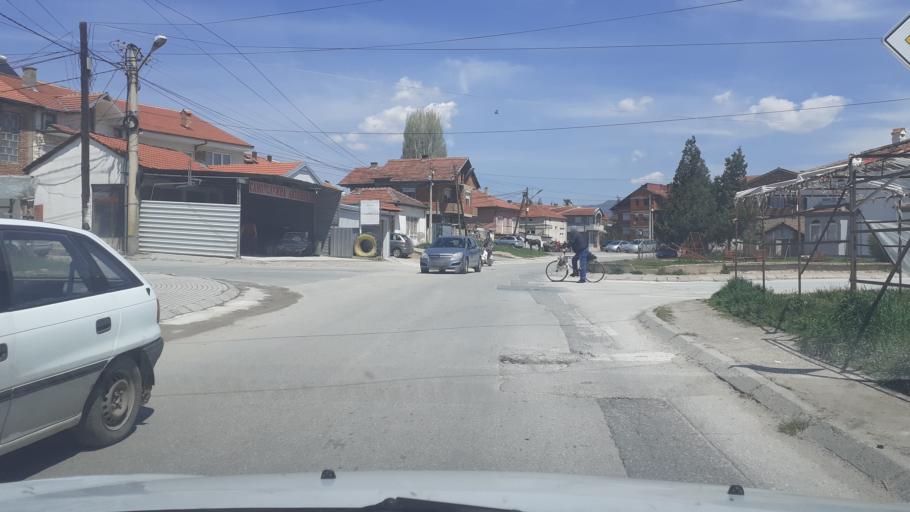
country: MK
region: Prilep
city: Prilep
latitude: 41.3512
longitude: 21.5554
